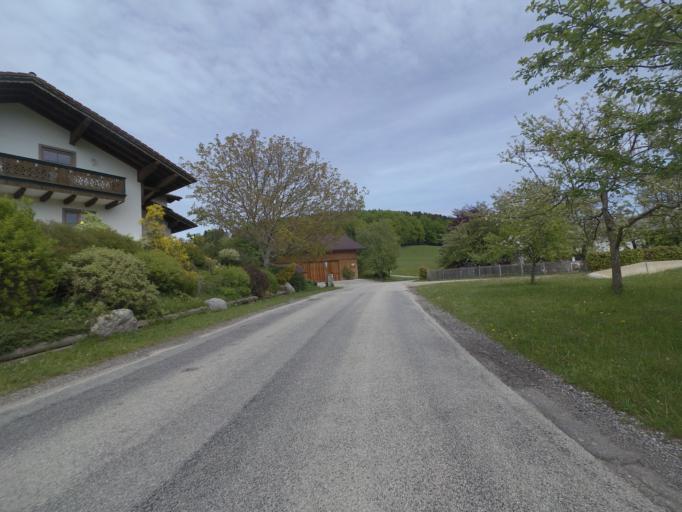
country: AT
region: Salzburg
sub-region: Politischer Bezirk Salzburg-Umgebung
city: Schleedorf
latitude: 47.9947
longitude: 13.1395
